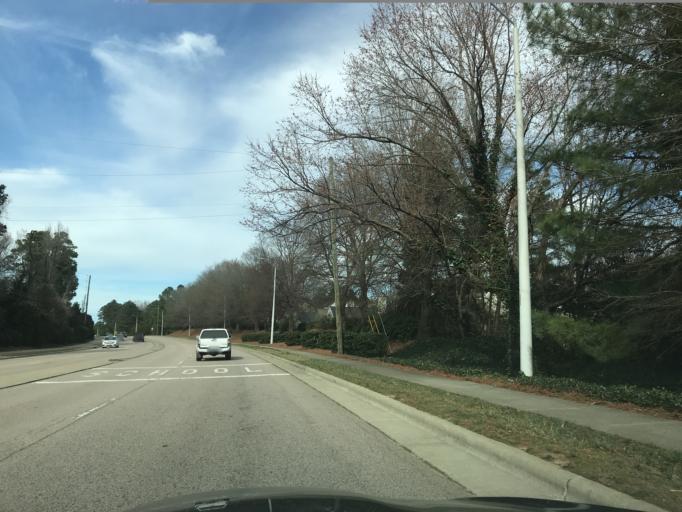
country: US
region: North Carolina
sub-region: Wake County
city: Morrisville
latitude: 35.8077
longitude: -78.8479
